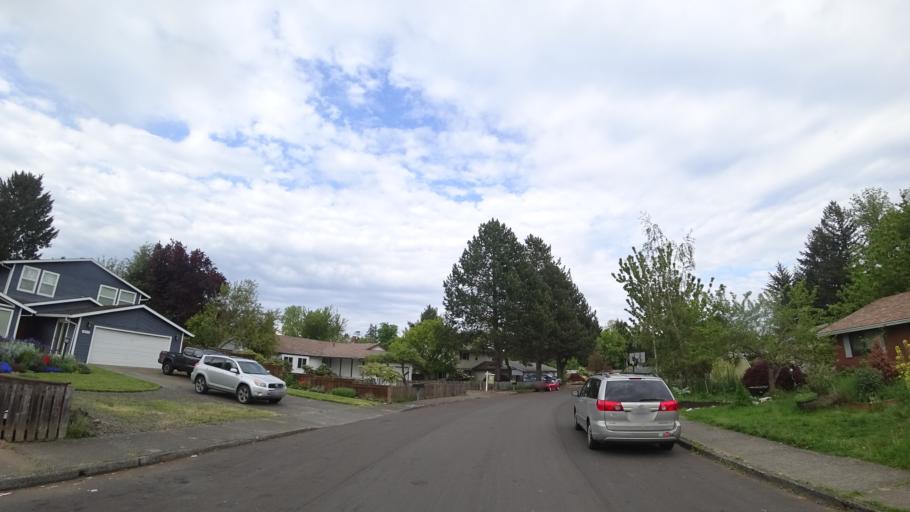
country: US
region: Oregon
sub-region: Washington County
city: Hillsboro
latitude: 45.4961
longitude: -122.9514
